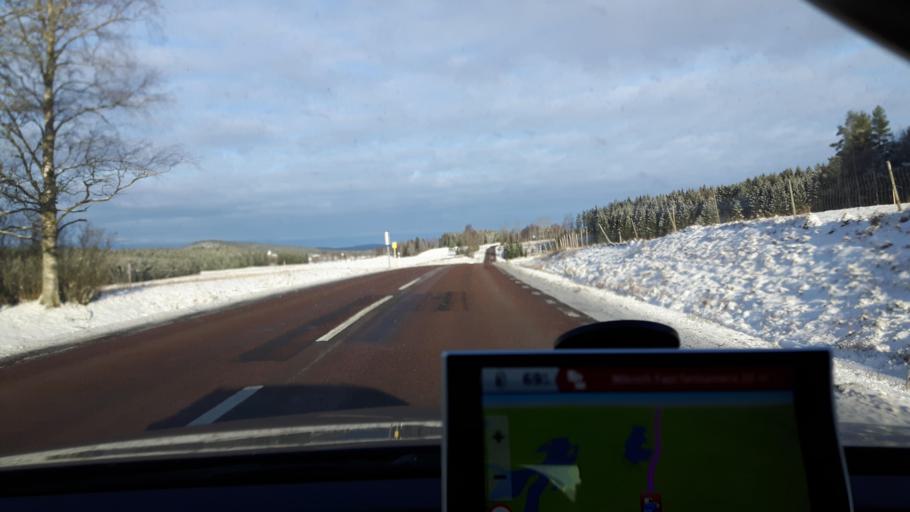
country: SE
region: Vaermland
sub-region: Karlstads Kommun
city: Edsvalla
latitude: 59.5479
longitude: 13.1958
